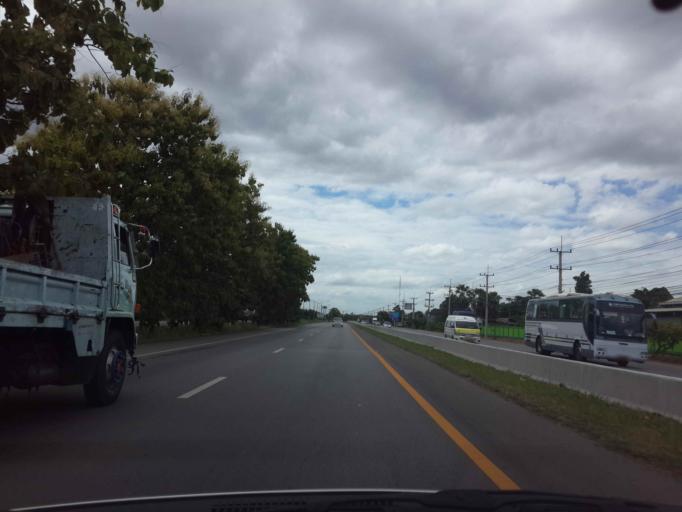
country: TH
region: Phetchaburi
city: Khao Yoi
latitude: 13.1565
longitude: 99.8481
